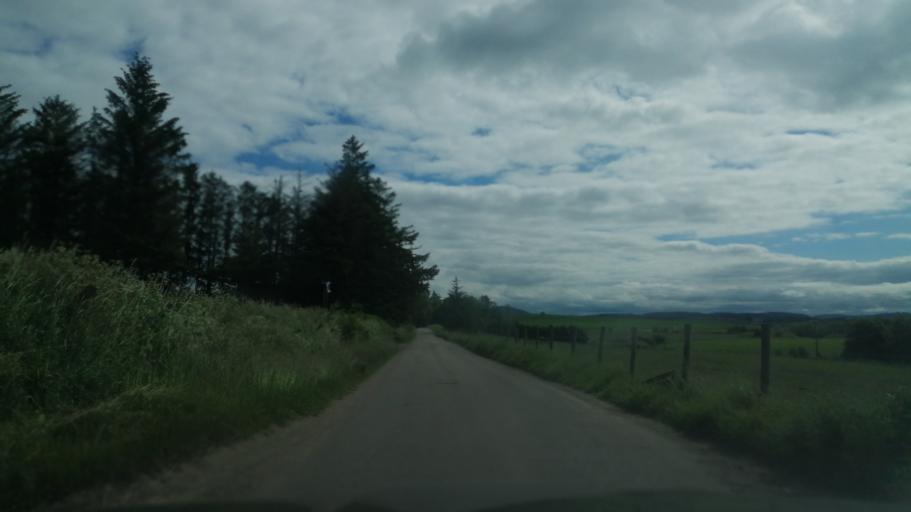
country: GB
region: Scotland
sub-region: Moray
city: Keith
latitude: 57.5566
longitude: -2.9429
